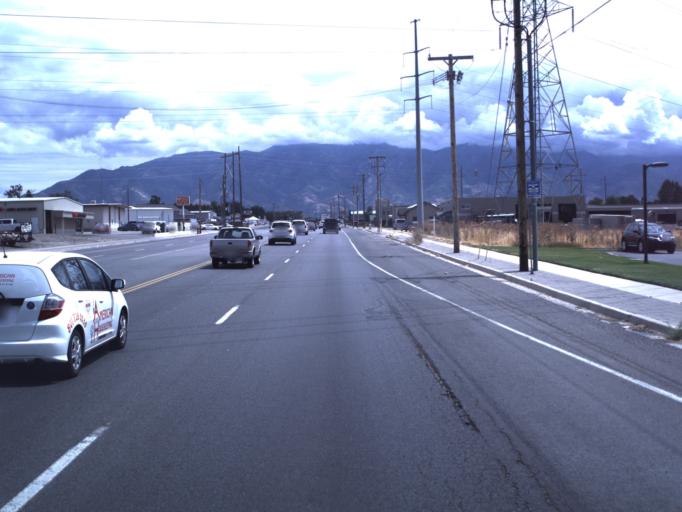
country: US
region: Utah
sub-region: Davis County
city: Syracuse
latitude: 41.0891
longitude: -112.0397
